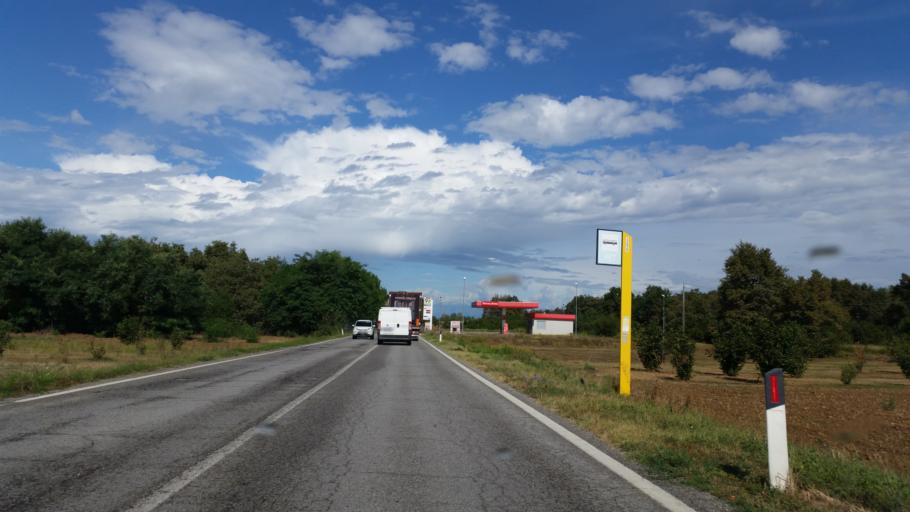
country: IT
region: Piedmont
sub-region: Provincia di Cuneo
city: Monta
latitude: 44.8273
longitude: 7.9351
